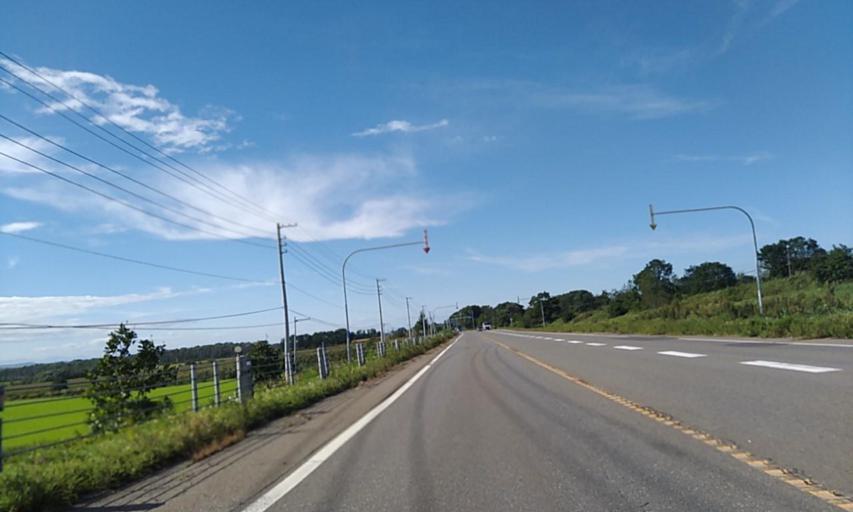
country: JP
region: Hokkaido
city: Obihiro
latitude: 42.7948
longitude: 143.5800
